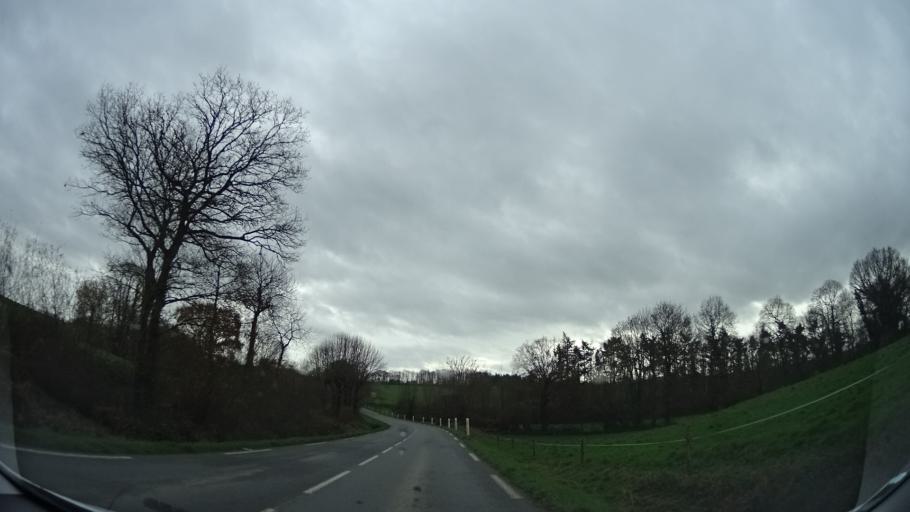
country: FR
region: Brittany
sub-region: Departement des Cotes-d'Armor
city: Les Champs-Geraux
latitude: 48.4192
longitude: -2.0014
